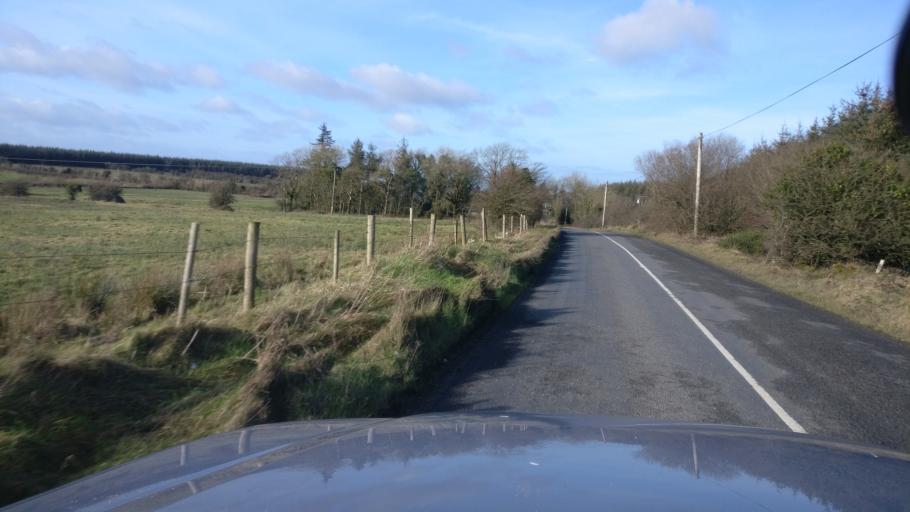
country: IE
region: Leinster
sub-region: Laois
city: Stradbally
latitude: 52.9254
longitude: -7.1942
